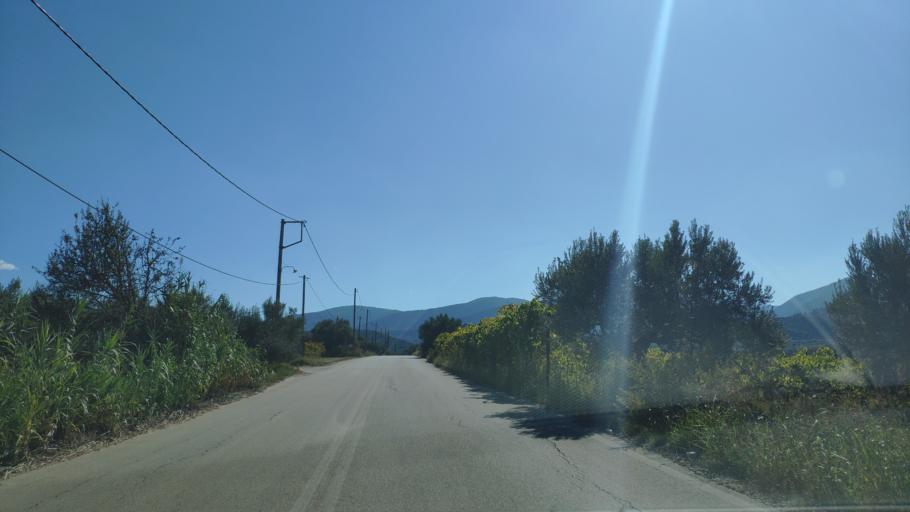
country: GR
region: Peloponnese
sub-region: Nomos Korinthias
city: Athikia
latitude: 37.8436
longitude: 22.9054
